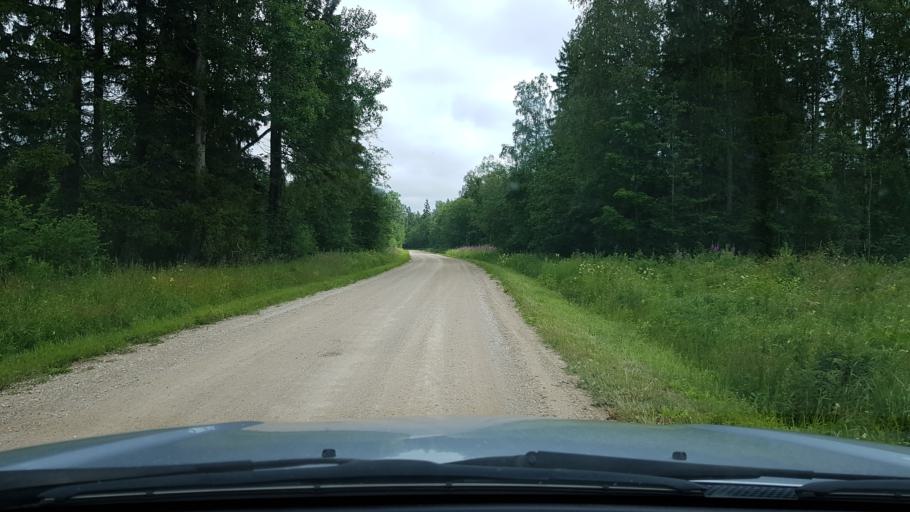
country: EE
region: Ida-Virumaa
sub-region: Narva-Joesuu linn
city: Narva-Joesuu
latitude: 59.3625
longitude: 28.0562
